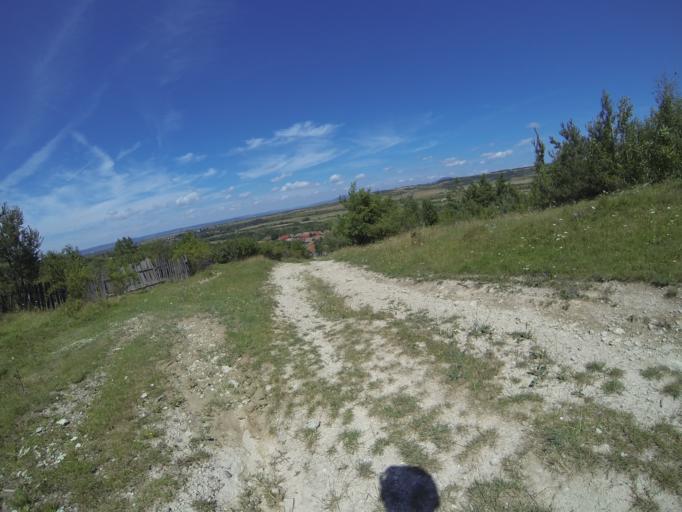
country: RO
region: Brasov
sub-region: Comuna Sinca Veche
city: Sinca Veche
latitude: 45.7508
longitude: 25.1762
